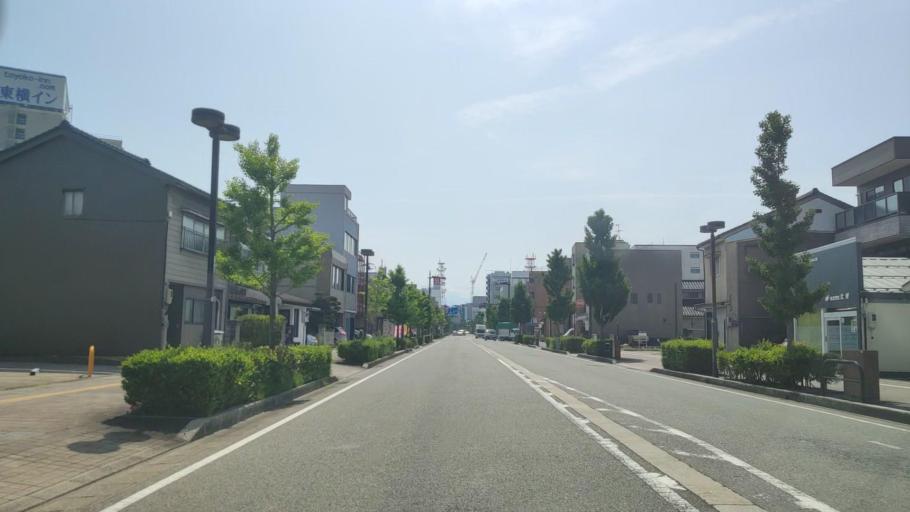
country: JP
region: Toyama
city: Toyama-shi
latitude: 36.6999
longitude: 137.2074
